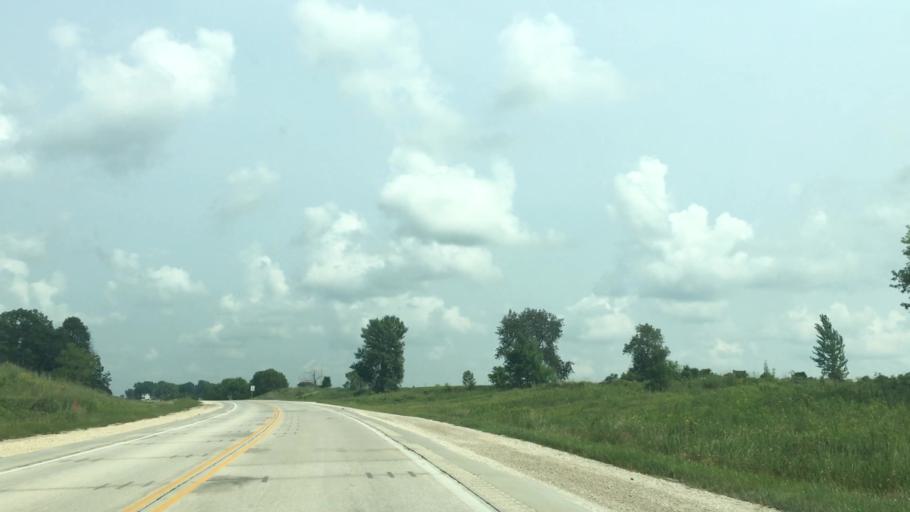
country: US
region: Iowa
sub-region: Winneshiek County
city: Decorah
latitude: 43.3467
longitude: -91.8062
